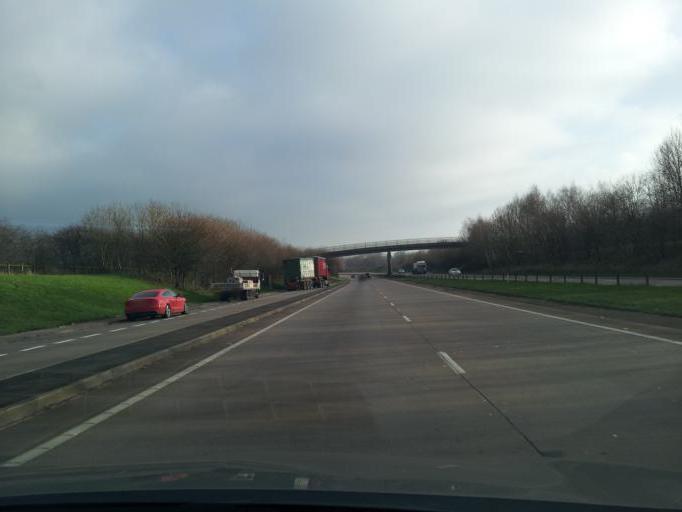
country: GB
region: England
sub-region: Staffordshire
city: Uttoxeter
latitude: 52.9068
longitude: -1.8157
